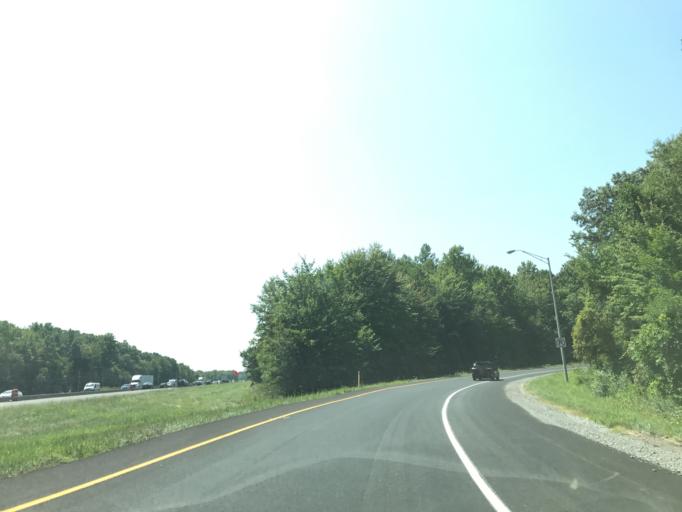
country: US
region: Indiana
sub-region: LaPorte County
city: Long Beach
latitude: 41.7363
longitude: -86.7892
